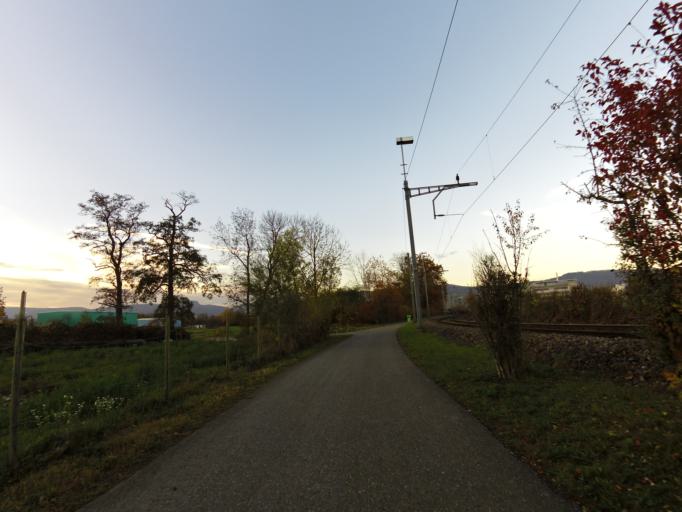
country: CH
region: Aargau
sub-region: Bezirk Aarau
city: Suhr
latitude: 47.3801
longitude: 8.0857
